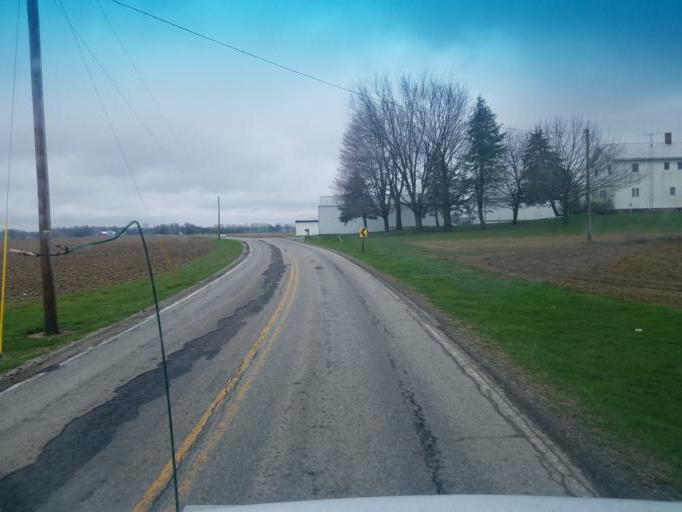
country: US
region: Ohio
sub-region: Richland County
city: Shelby
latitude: 40.9266
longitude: -82.6446
